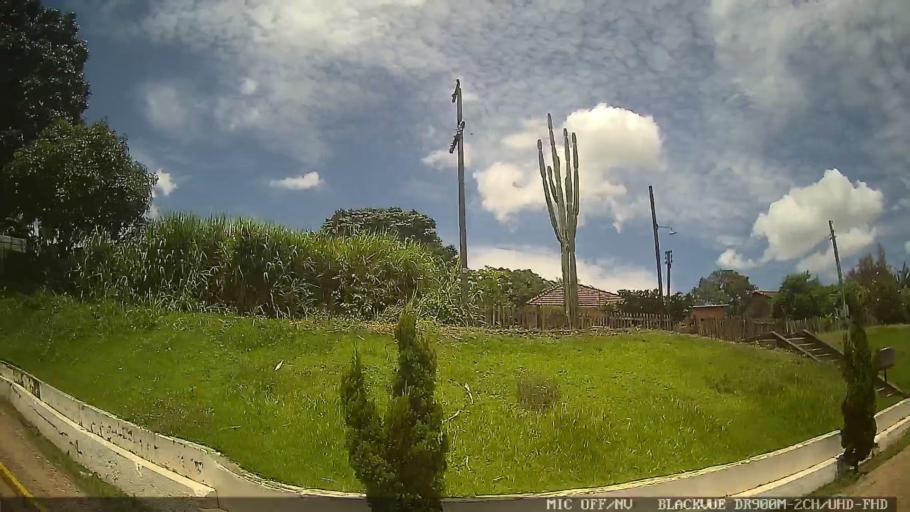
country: BR
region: Sao Paulo
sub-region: Laranjal Paulista
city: Laranjal Paulista
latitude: -23.0460
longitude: -47.8385
